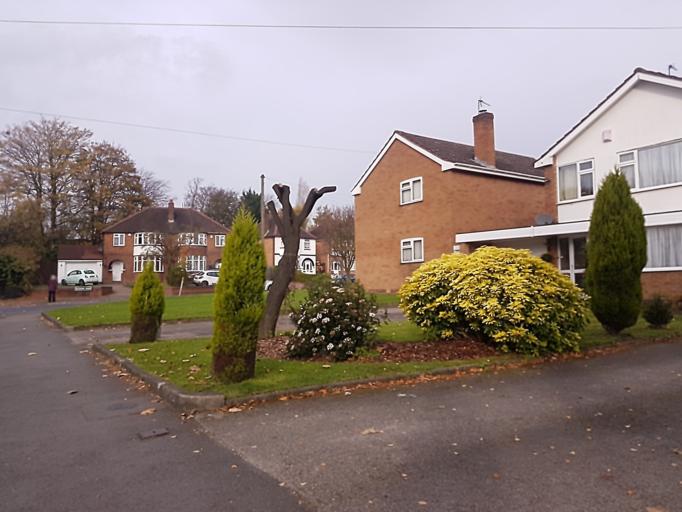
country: GB
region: England
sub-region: City and Borough of Birmingham
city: Acocks Green
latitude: 52.4374
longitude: -1.8022
